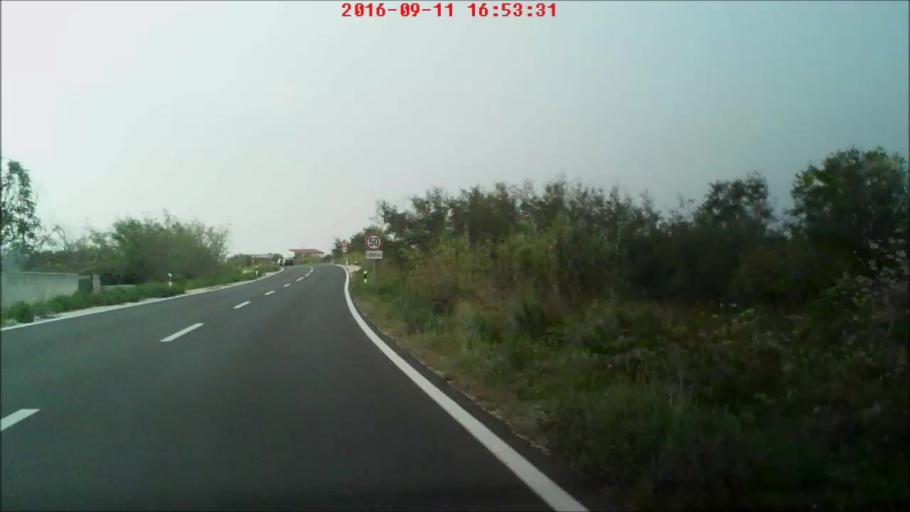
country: HR
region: Zadarska
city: Nin
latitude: 44.2482
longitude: 15.1647
